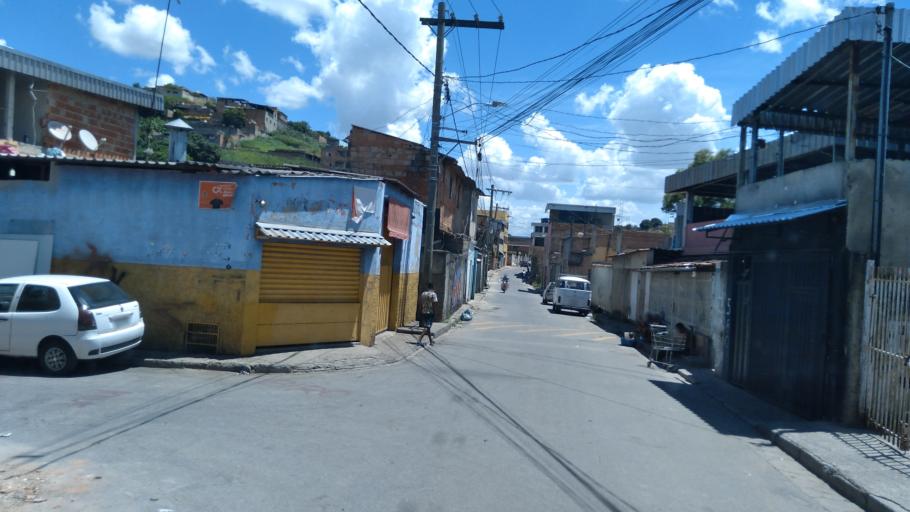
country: BR
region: Minas Gerais
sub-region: Santa Luzia
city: Santa Luzia
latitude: -19.8343
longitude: -43.8941
